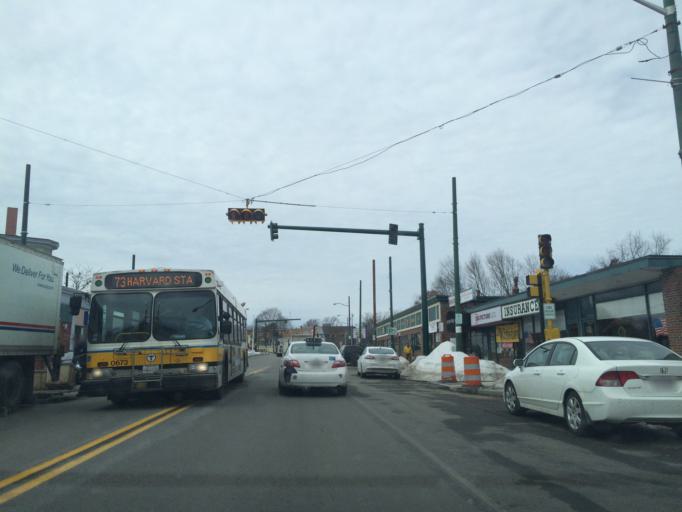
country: US
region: Massachusetts
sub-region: Middlesex County
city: Belmont
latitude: 42.3874
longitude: -71.1891
